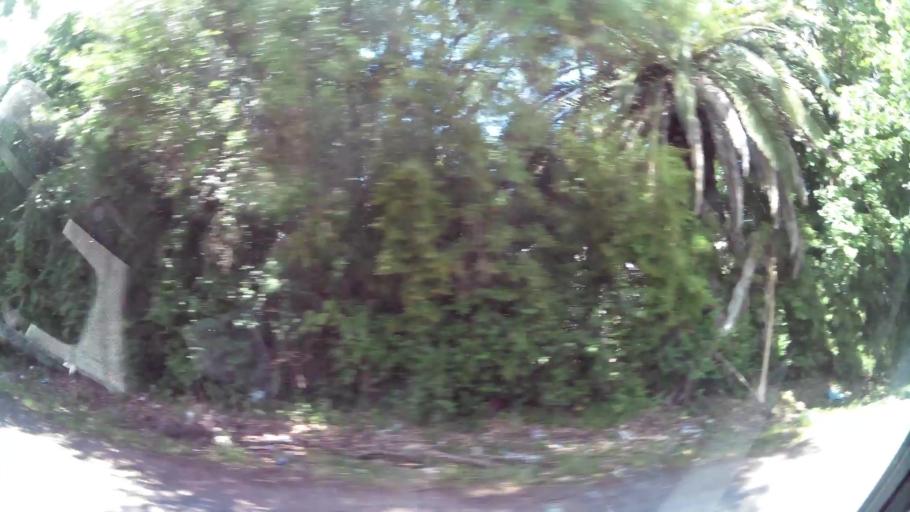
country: AR
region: Buenos Aires
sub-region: Partido de Tigre
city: Tigre
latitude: -34.4126
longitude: -58.5964
